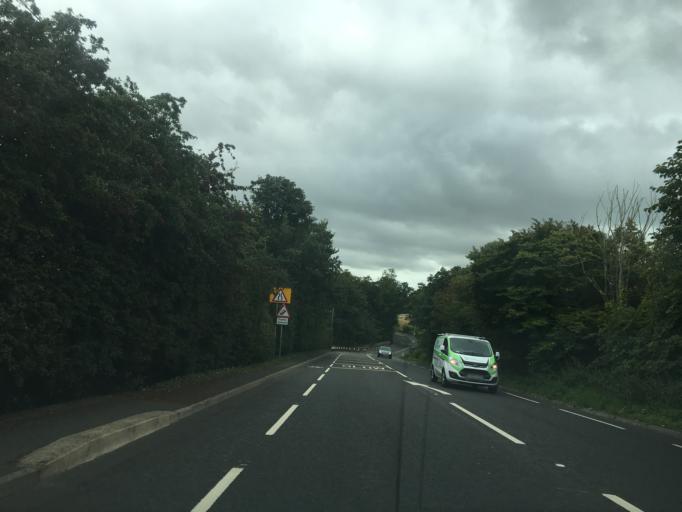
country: GB
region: Scotland
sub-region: Midlothian
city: Dalkeith
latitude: 55.8932
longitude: -3.0881
